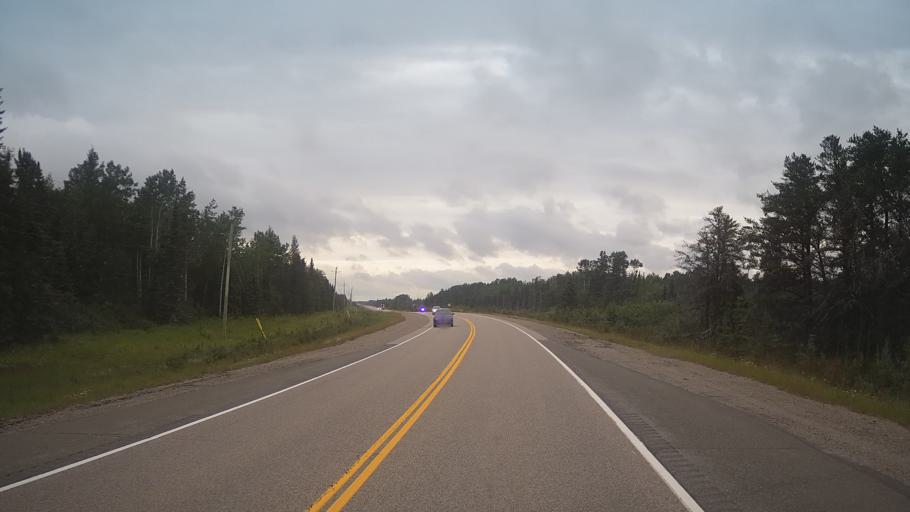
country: CA
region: Ontario
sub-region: Thunder Bay District
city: Thunder Bay
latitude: 48.8419
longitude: -89.9411
